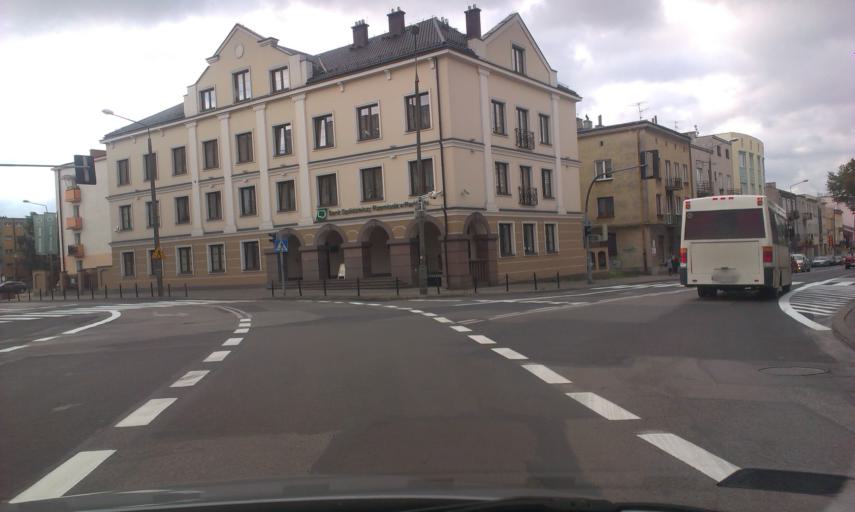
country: PL
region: Masovian Voivodeship
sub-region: Radom
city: Radom
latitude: 51.3955
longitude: 21.1546
